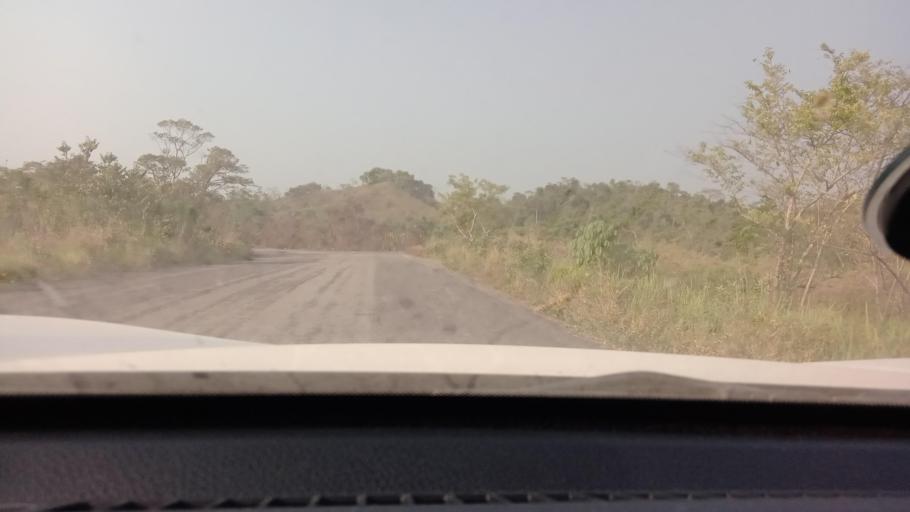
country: MX
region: Tabasco
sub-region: Huimanguillo
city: Francisco Rueda
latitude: 17.6692
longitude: -93.8672
